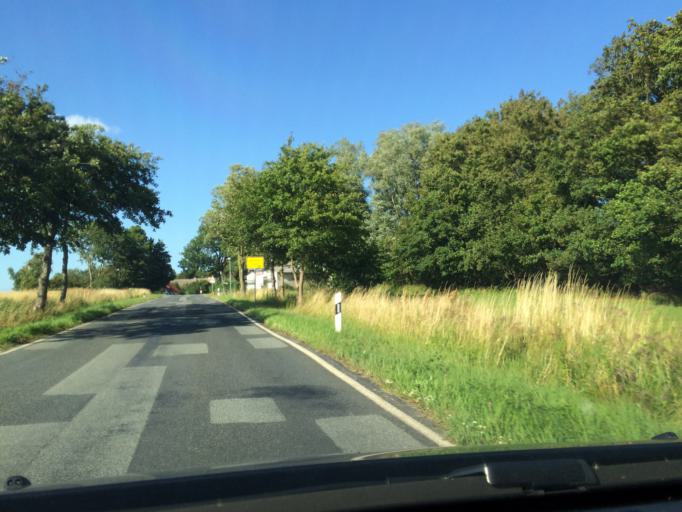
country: DE
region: Mecklenburg-Vorpommern
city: Altenpleen
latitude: 54.3844
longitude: 12.9437
